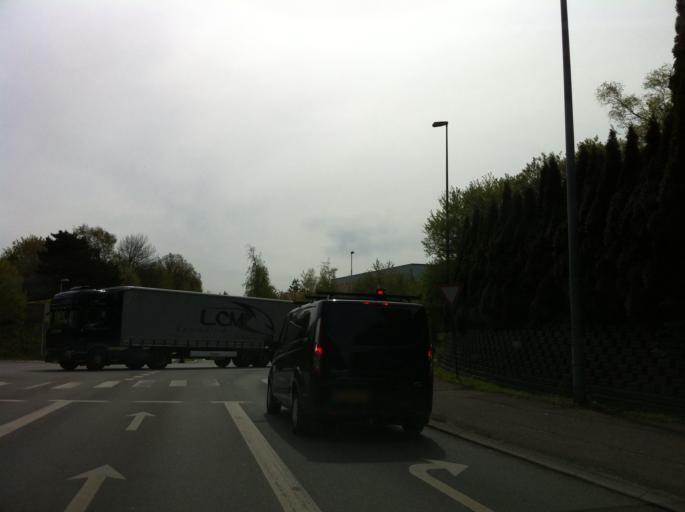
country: DK
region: Capital Region
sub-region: Allerod Kommune
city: Lillerod
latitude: 55.8699
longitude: 12.3592
